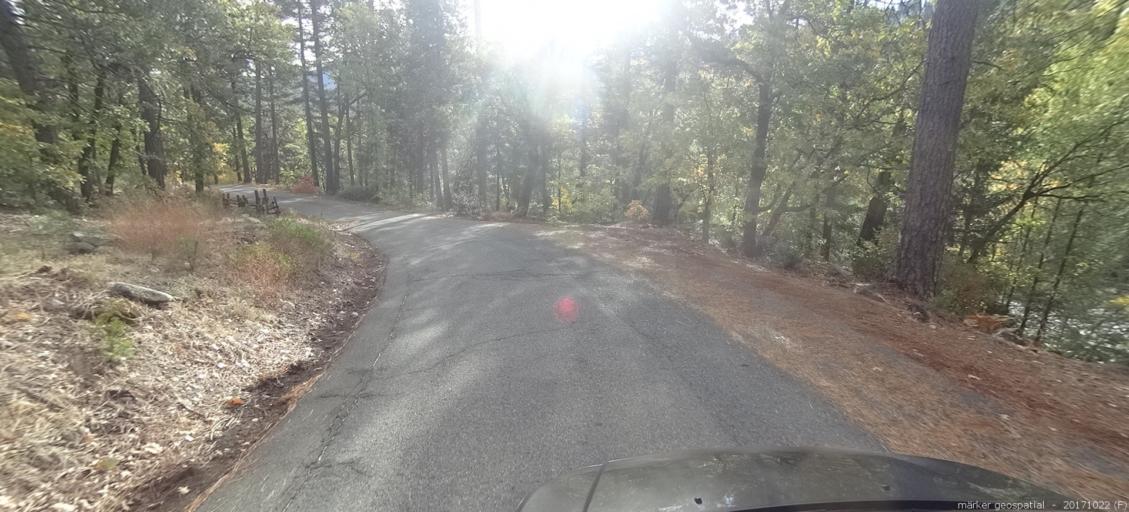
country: US
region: California
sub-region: Siskiyou County
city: Dunsmuir
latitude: 41.1476
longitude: -122.3318
